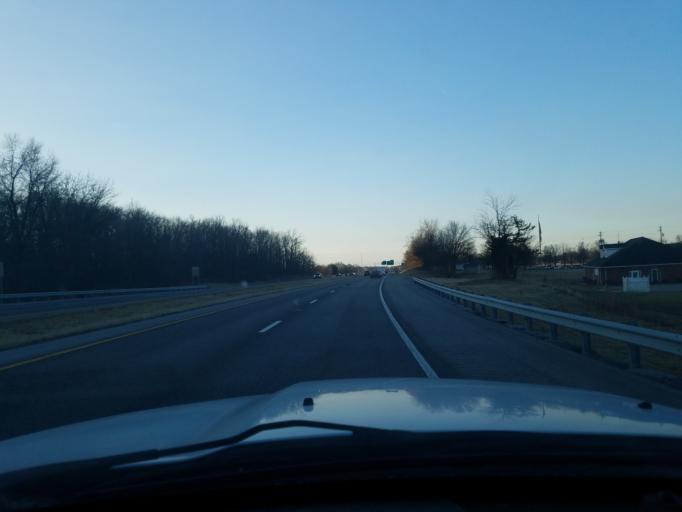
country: US
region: Kentucky
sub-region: Henderson County
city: Henderson
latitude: 37.8371
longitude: -87.5647
